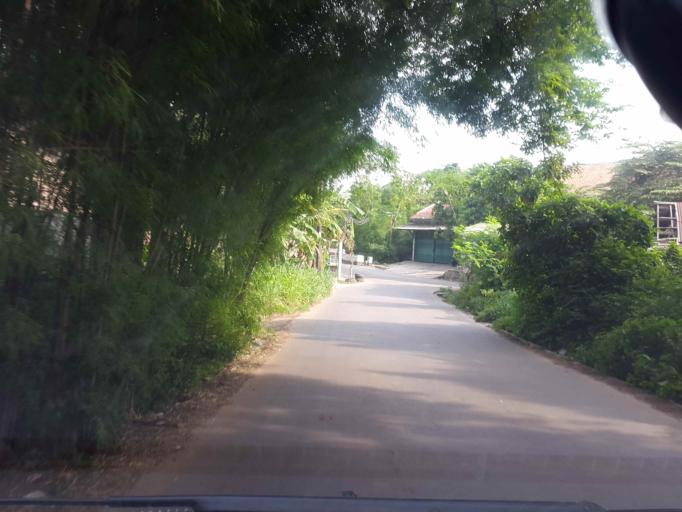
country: ID
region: West Java
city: Ciputat
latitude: -6.2606
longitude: 106.6767
